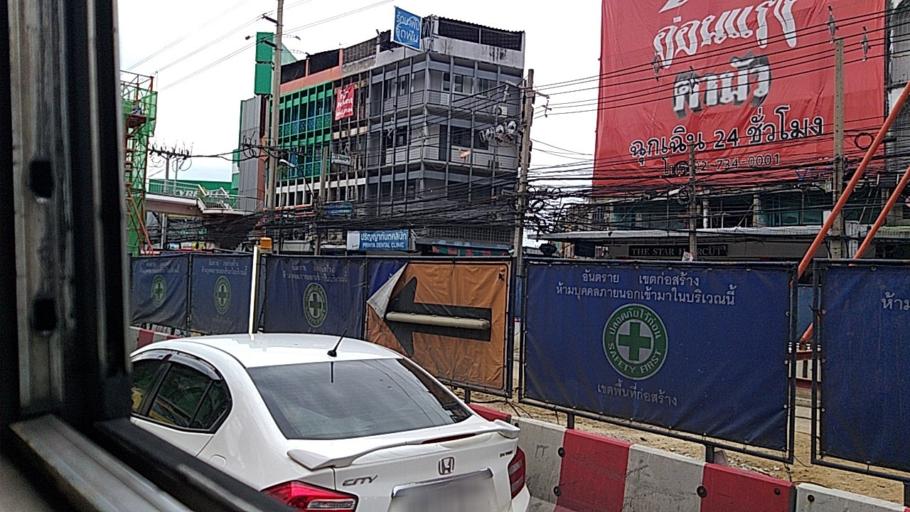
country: TH
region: Bangkok
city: Bang Kapi
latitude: 13.7750
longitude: 100.6376
